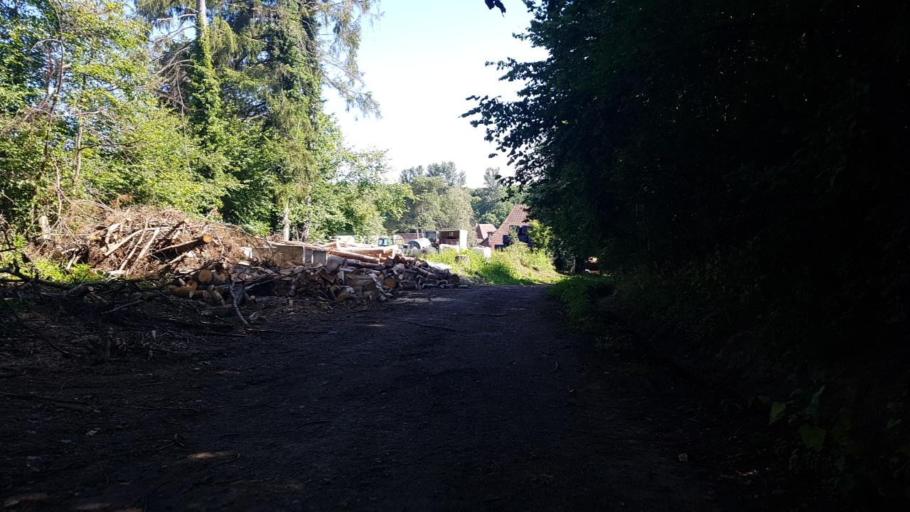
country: FR
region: Nord-Pas-de-Calais
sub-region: Departement du Nord
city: Anor
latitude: 49.9722
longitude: 4.1199
